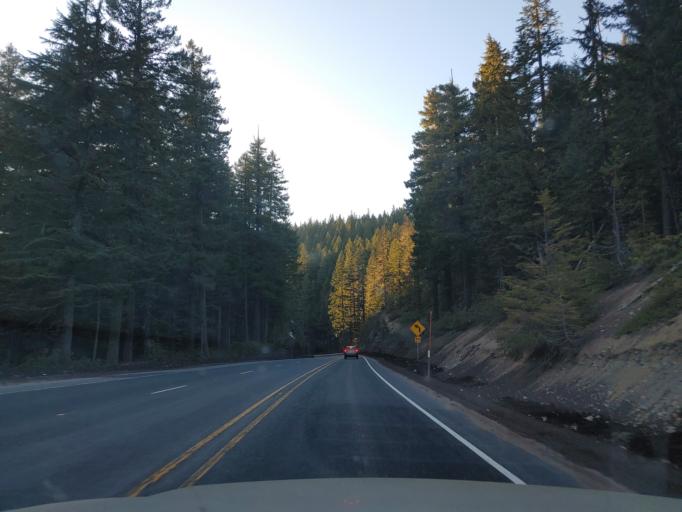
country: US
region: Oregon
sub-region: Lane County
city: Oakridge
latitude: 43.6121
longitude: -122.1252
